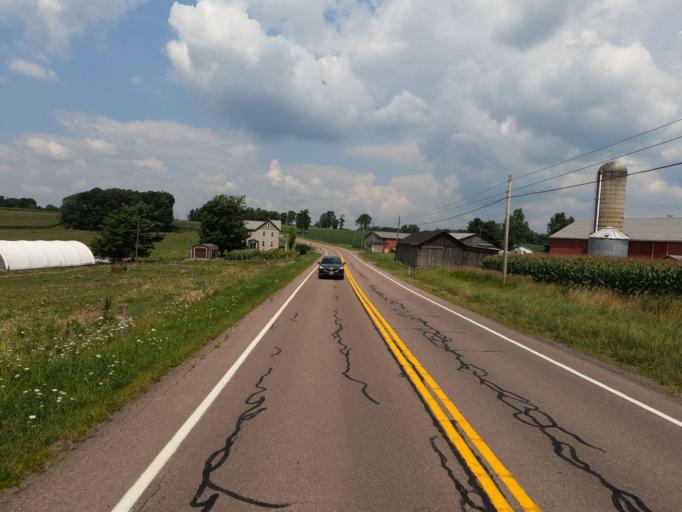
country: US
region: Maryland
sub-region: Allegany County
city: Westernport
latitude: 39.6152
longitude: -79.2154
